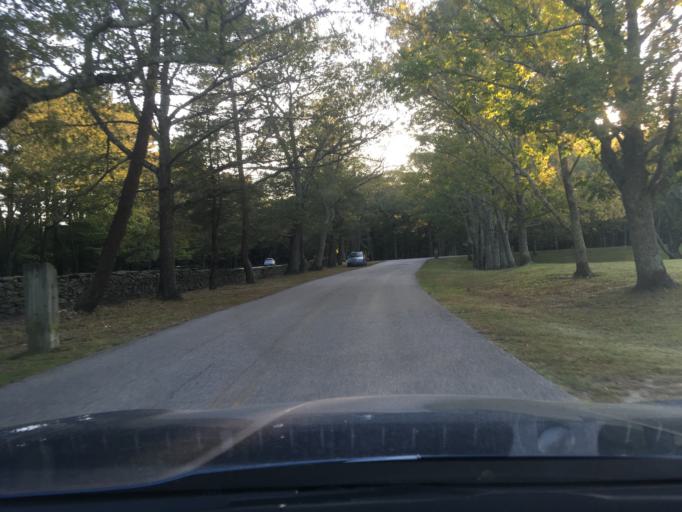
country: US
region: Rhode Island
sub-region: Kent County
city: East Greenwich
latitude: 41.6529
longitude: -71.4400
